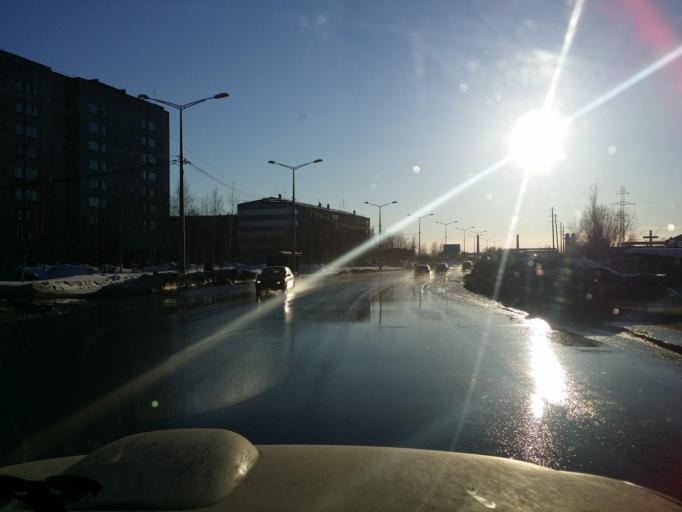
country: RU
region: Khanty-Mansiyskiy Avtonomnyy Okrug
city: Nizhnevartovsk
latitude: 60.9489
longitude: 76.5536
